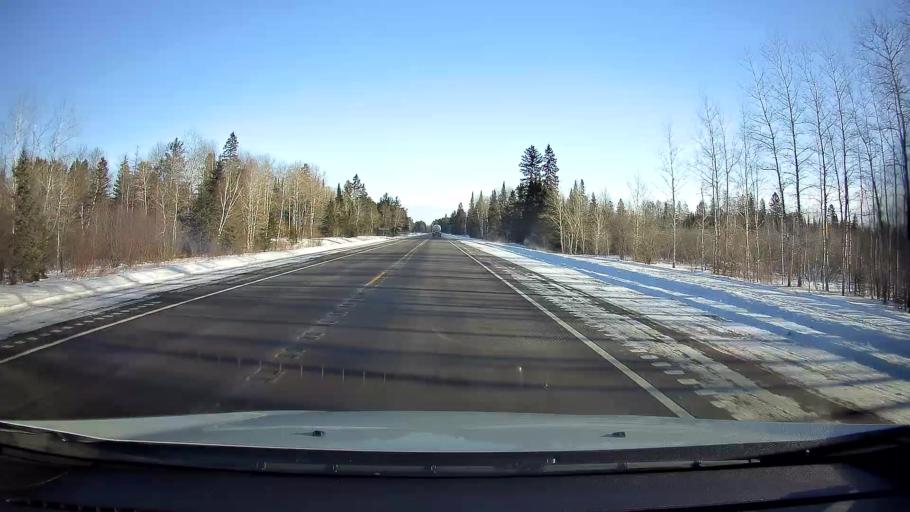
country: US
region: Wisconsin
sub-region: Sawyer County
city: Hayward
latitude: 46.0797
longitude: -91.4035
